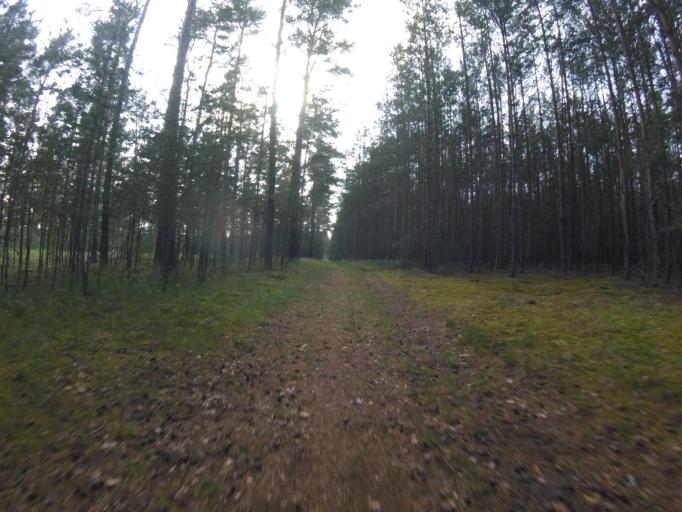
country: DE
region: Brandenburg
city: Halbe
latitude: 52.1103
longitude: 13.7405
